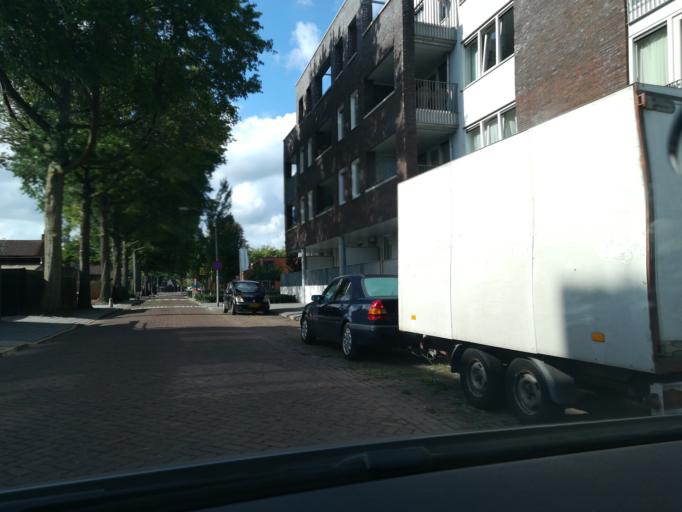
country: NL
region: North Brabant
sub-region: Gemeente Valkenswaard
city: Valkenswaard
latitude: 51.3592
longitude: 5.4559
